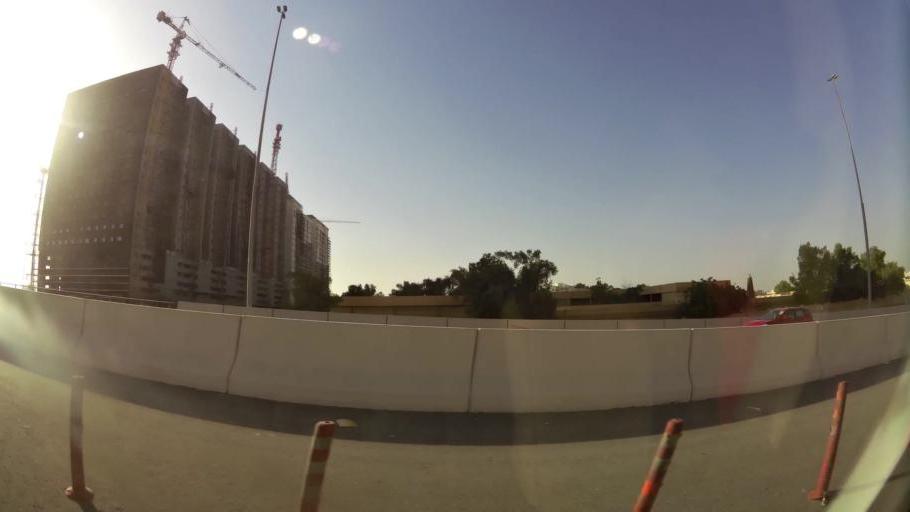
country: AE
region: Ajman
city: Ajman
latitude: 25.3946
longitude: 55.4853
